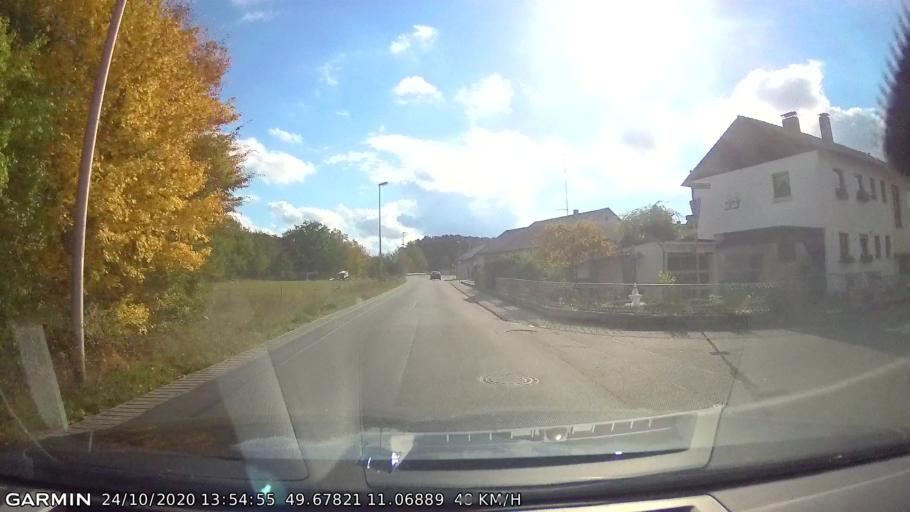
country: DE
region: Bavaria
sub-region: Upper Franconia
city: Poxdorf
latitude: 49.6782
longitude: 11.0689
